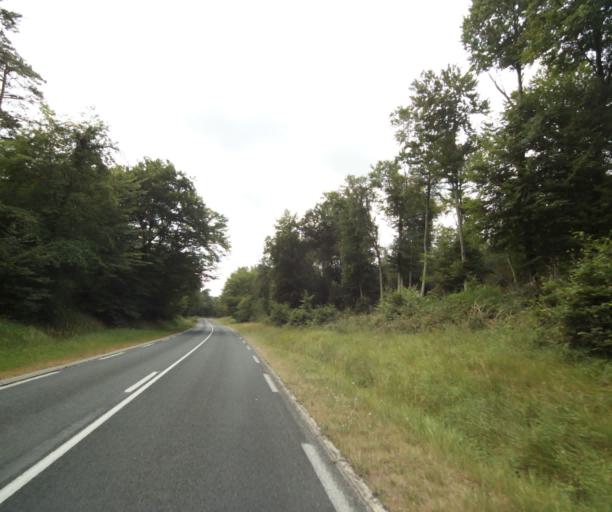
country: FR
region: Ile-de-France
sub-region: Departement de Seine-et-Marne
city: Barbizon
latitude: 48.4153
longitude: 2.6297
